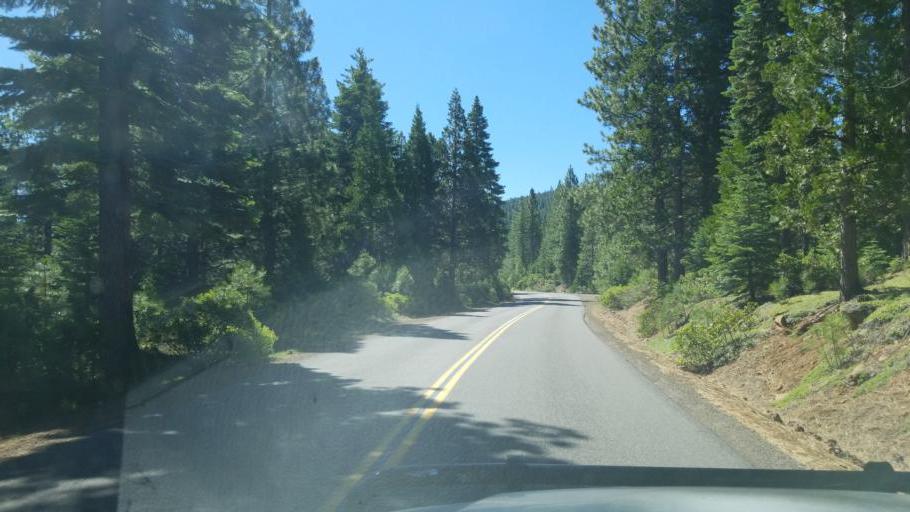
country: US
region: California
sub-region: Lassen County
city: Susanville
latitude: 40.5151
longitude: -120.7810
